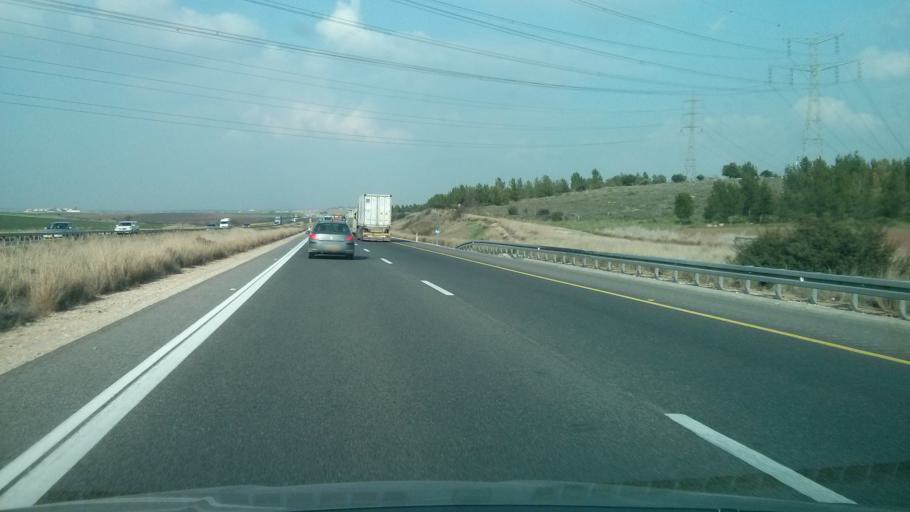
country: IL
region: Southern District
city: Qiryat Gat
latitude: 31.6859
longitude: 34.8100
